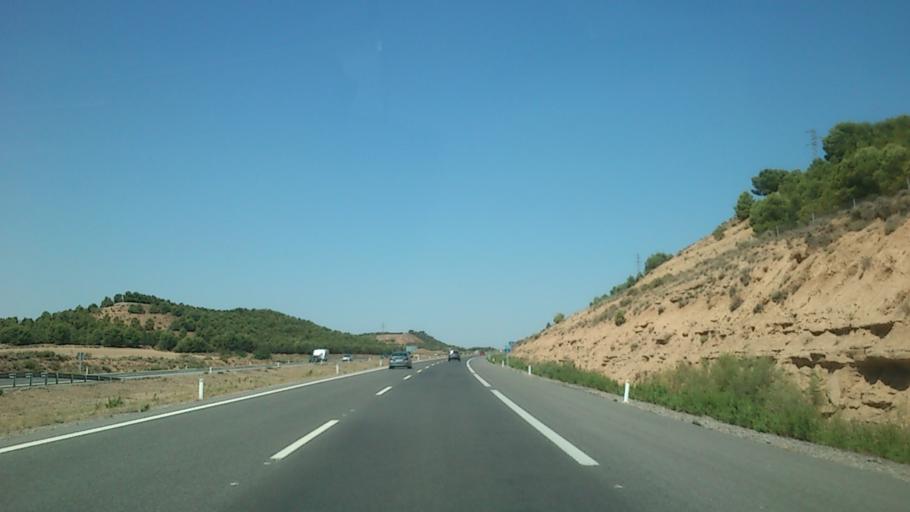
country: ES
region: Navarre
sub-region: Provincia de Navarra
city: Murchante
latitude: 42.0786
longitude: -1.7030
